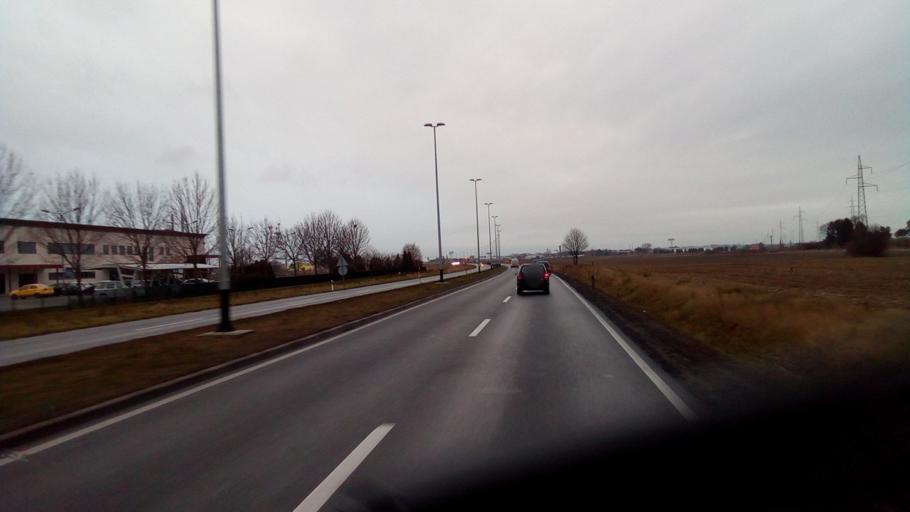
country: HR
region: Varazdinska
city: Varazdin
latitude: 46.2751
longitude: 16.3612
